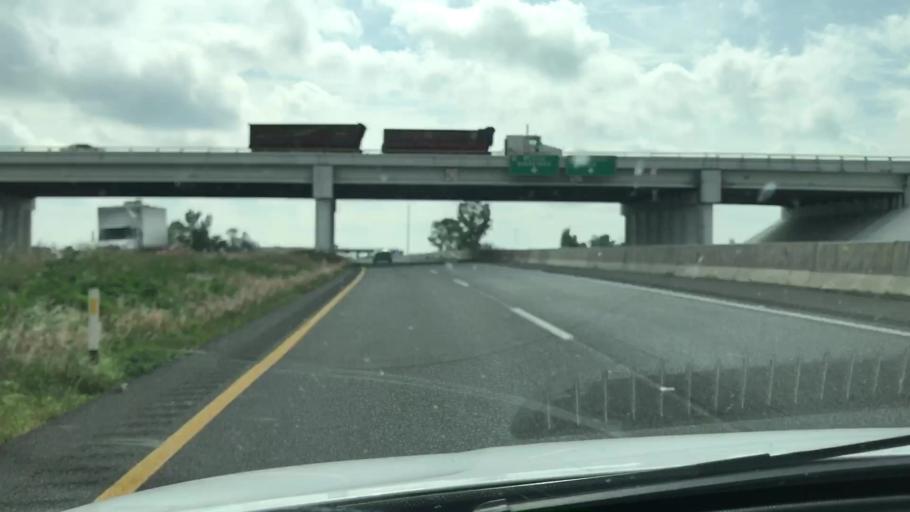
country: MX
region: Guanajuato
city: Cerro Gordo
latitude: 20.5911
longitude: -101.1442
